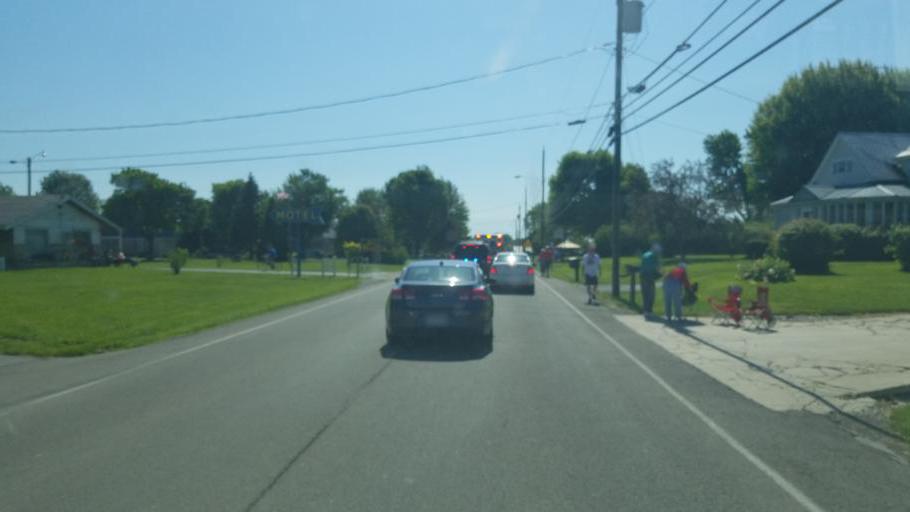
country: US
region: Ohio
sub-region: Hardin County
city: Kenton
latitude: 40.6453
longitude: -83.5944
